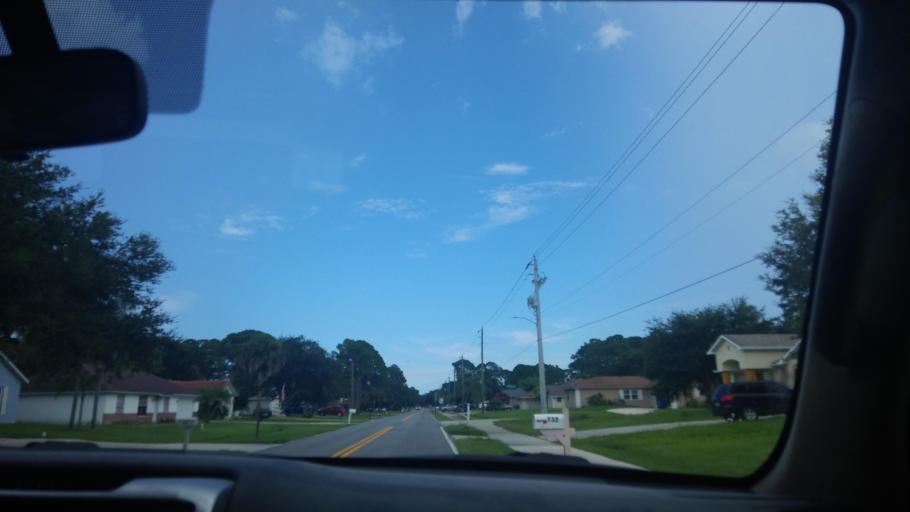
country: US
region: Florida
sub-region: Brevard County
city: West Melbourne
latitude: 28.0100
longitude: -80.6521
